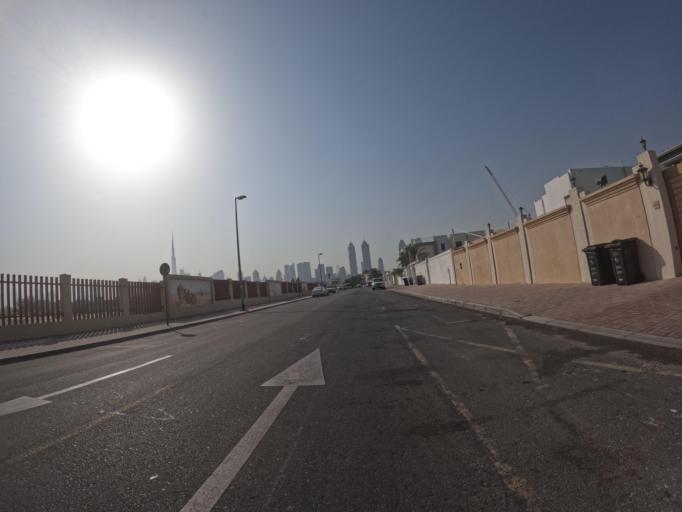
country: AE
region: Dubai
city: Dubai
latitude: 25.1955
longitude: 55.2407
